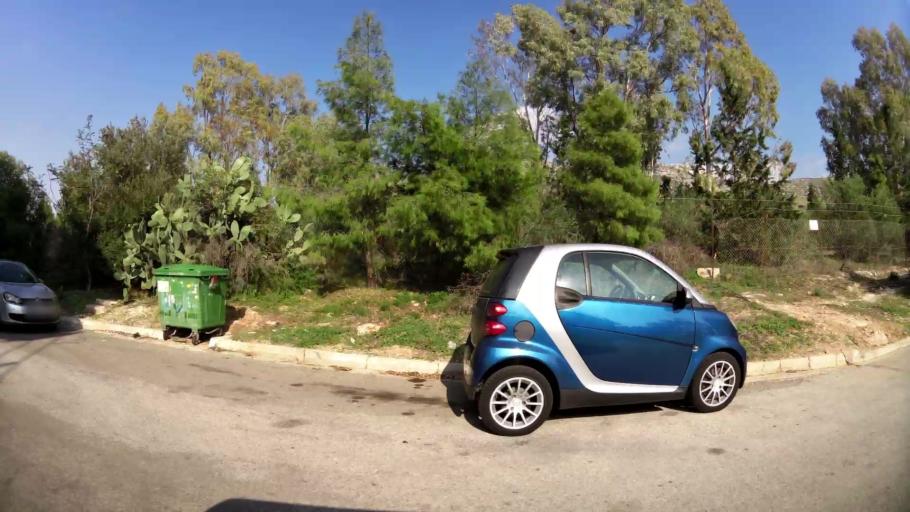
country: GR
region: Attica
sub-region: Nomarchia Athinas
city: Argyroupoli
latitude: 37.9109
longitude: 23.7585
